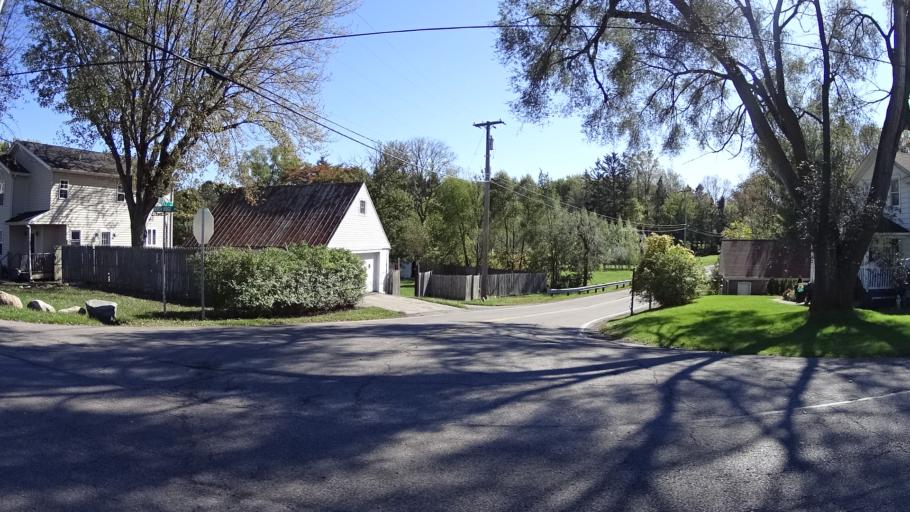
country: US
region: Ohio
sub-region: Lorain County
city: Amherst
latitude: 41.4085
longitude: -82.2009
